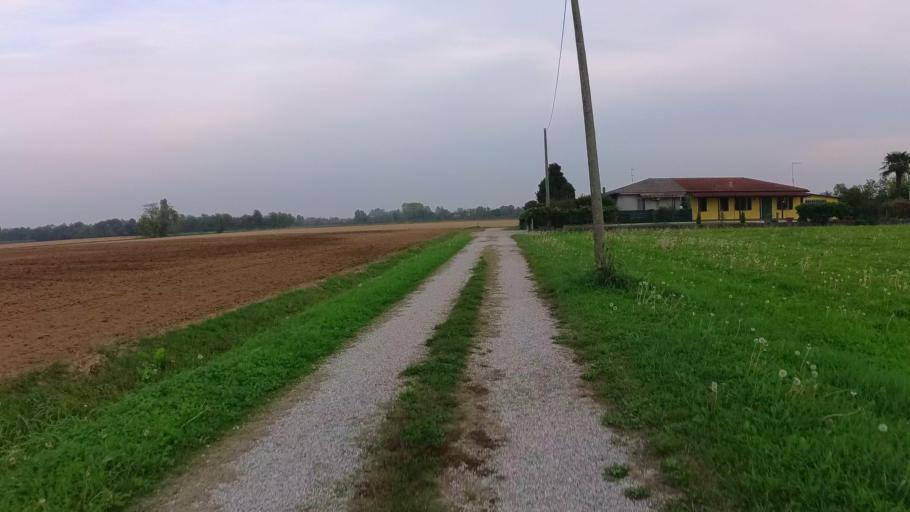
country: IT
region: Veneto
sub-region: Provincia di Padova
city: Bosco
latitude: 45.4381
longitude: 11.7954
